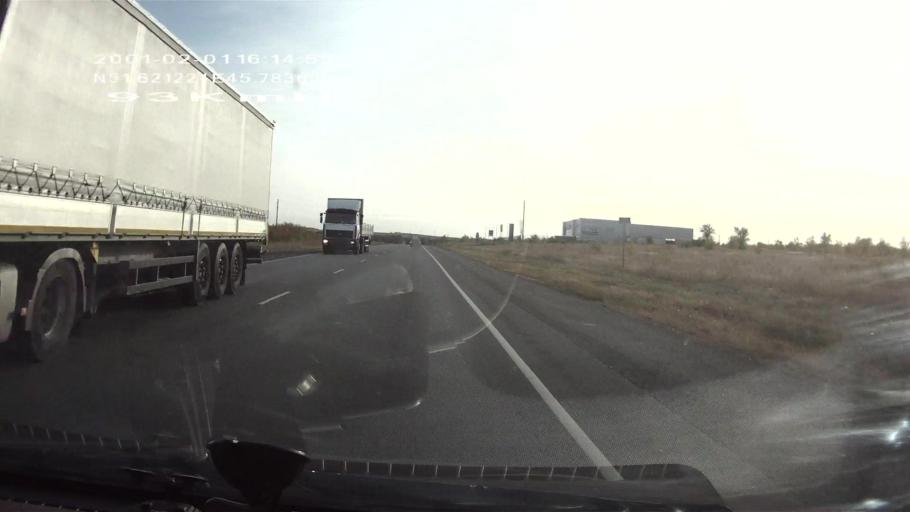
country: RU
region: Saratov
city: Sokolovyy
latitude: 51.6211
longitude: 45.7834
